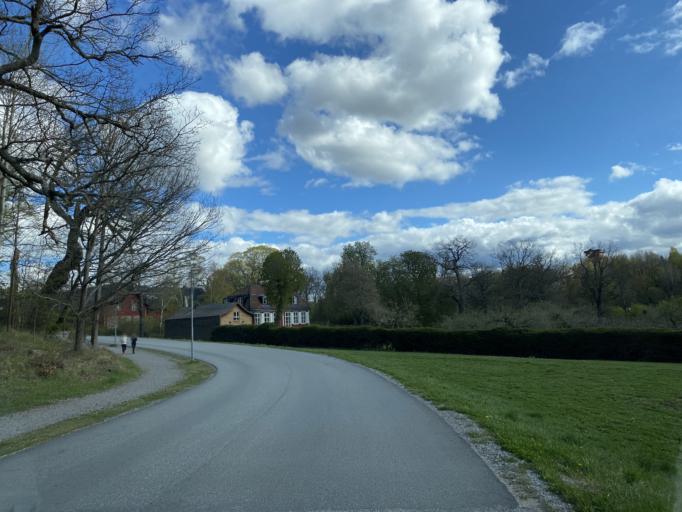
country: SE
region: Stockholm
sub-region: Stockholms Kommun
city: OEstermalm
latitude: 59.3629
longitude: 18.0749
